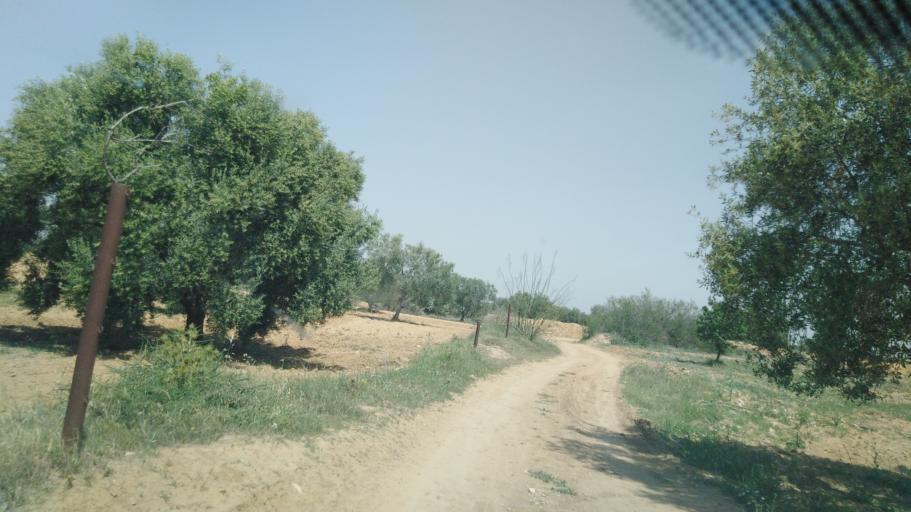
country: TN
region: Safaqis
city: Sfax
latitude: 34.7337
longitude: 10.5744
